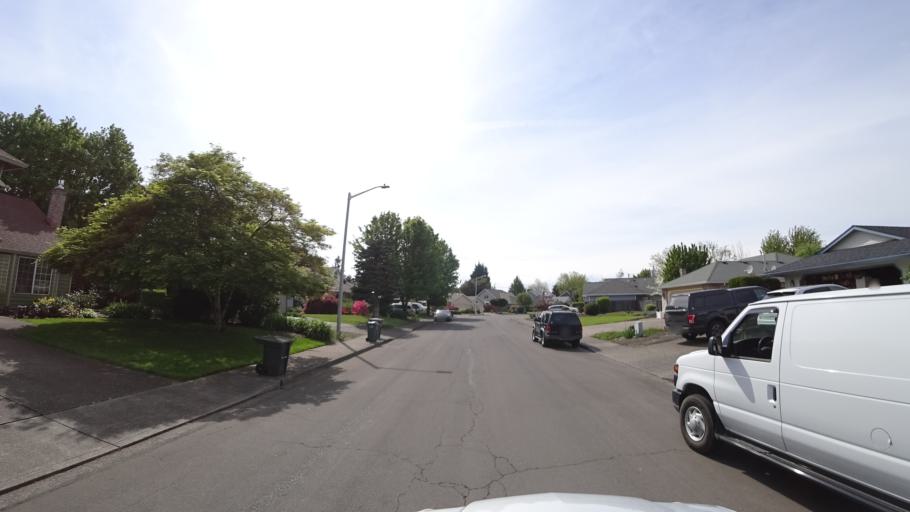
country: US
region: Oregon
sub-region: Washington County
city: Rockcreek
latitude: 45.5349
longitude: -122.9275
